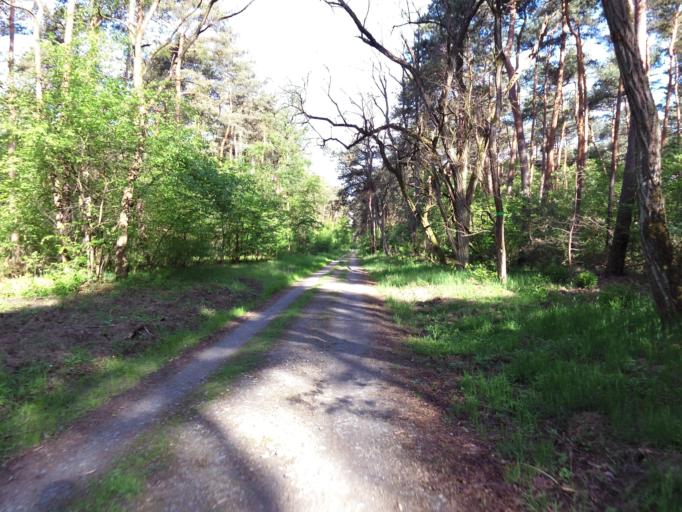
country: DE
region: Hesse
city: Lampertheim
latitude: 49.6153
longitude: 8.5058
